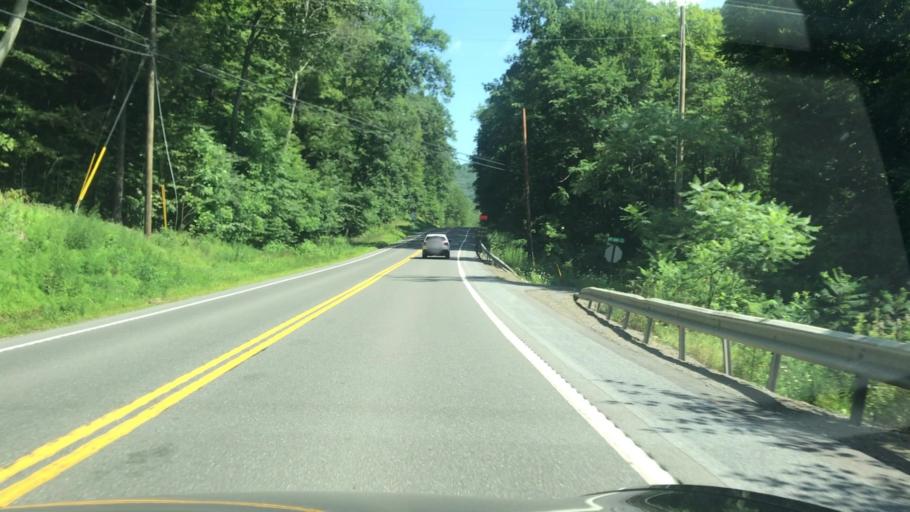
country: US
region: Pennsylvania
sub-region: Tioga County
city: Blossburg
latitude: 41.4767
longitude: -76.9806
